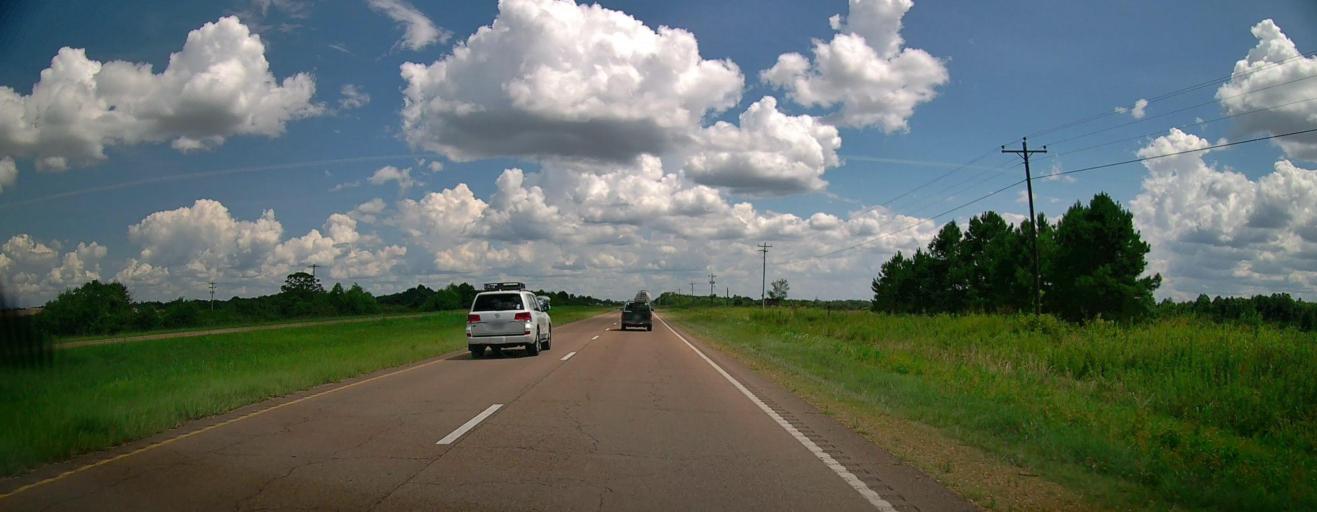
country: US
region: Mississippi
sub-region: Lowndes County
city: Columbus Air Force Base
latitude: 33.6959
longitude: -88.4418
